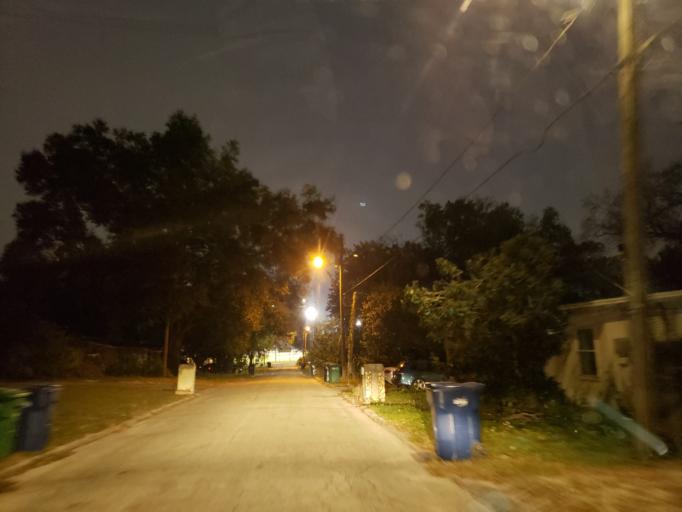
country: US
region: Florida
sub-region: Hillsborough County
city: University
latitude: 28.0283
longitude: -82.4362
